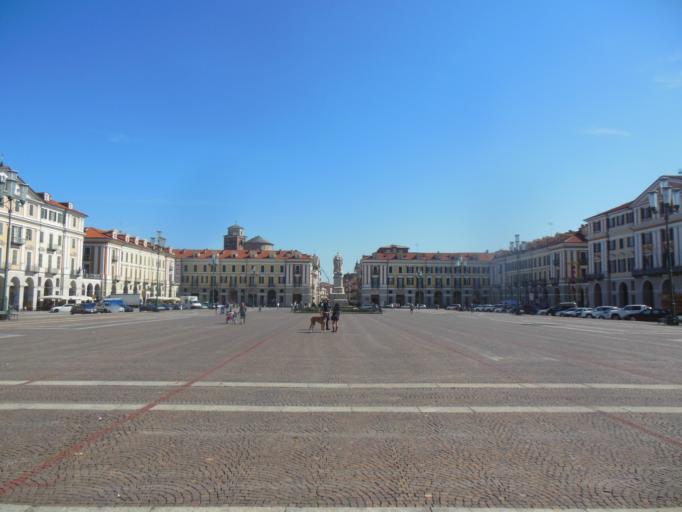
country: IT
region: Piedmont
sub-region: Provincia di Cuneo
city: Cuneo
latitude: 44.3887
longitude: 7.5472
